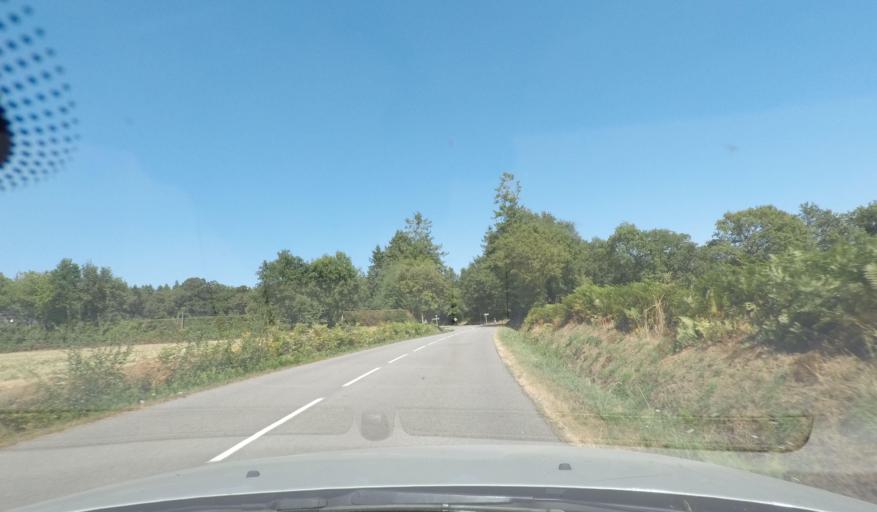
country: FR
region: Brittany
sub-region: Departement du Morbihan
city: Caro
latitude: 47.8294
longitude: -2.3422
